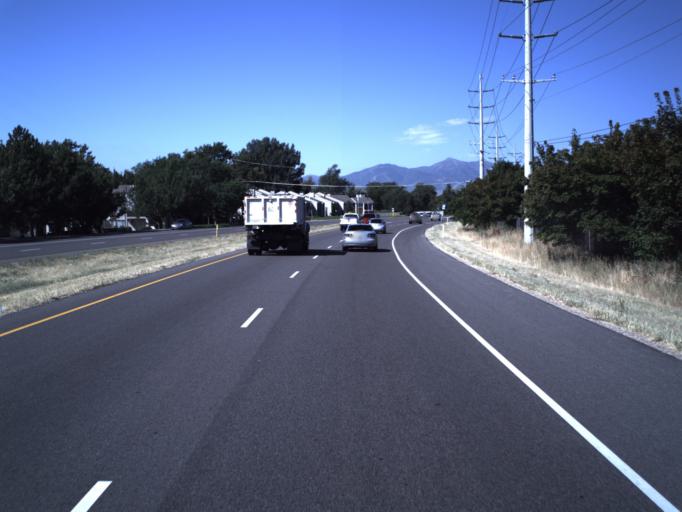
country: US
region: Utah
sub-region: Salt Lake County
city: Taylorsville
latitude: 40.6684
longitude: -111.9331
